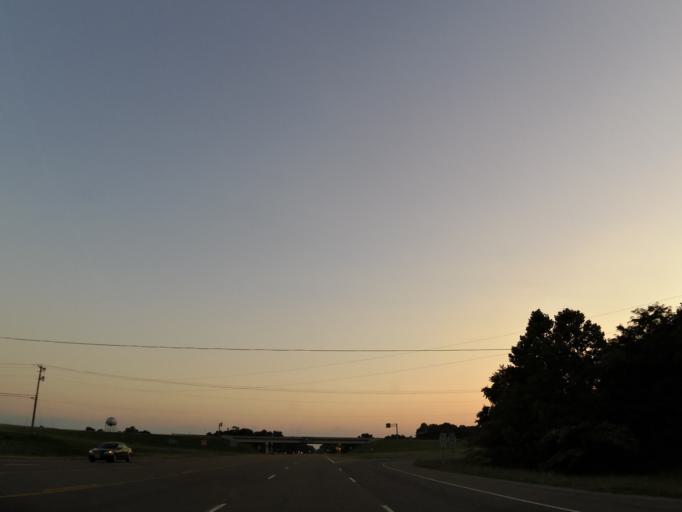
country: US
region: Tennessee
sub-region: Carroll County
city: McKenzie
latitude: 36.1425
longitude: -88.4862
